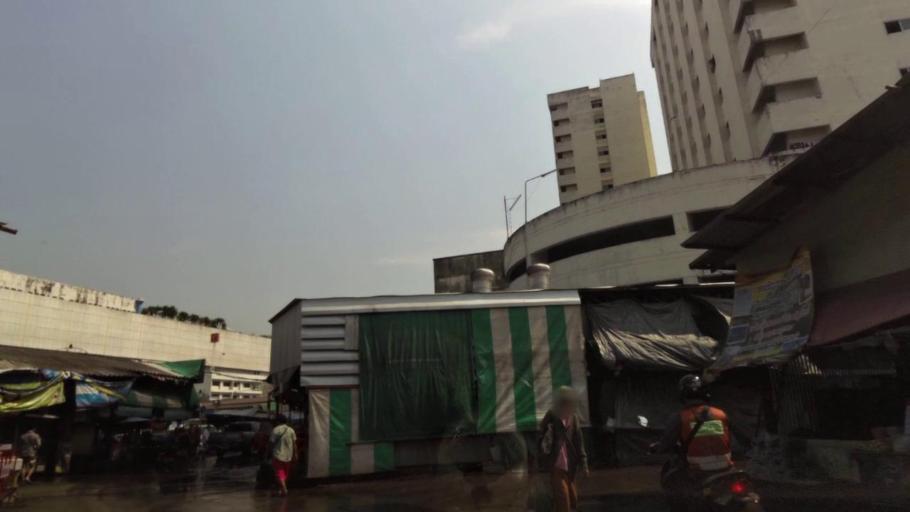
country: TH
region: Samut Prakan
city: Samut Prakan
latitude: 13.6494
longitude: 100.5941
